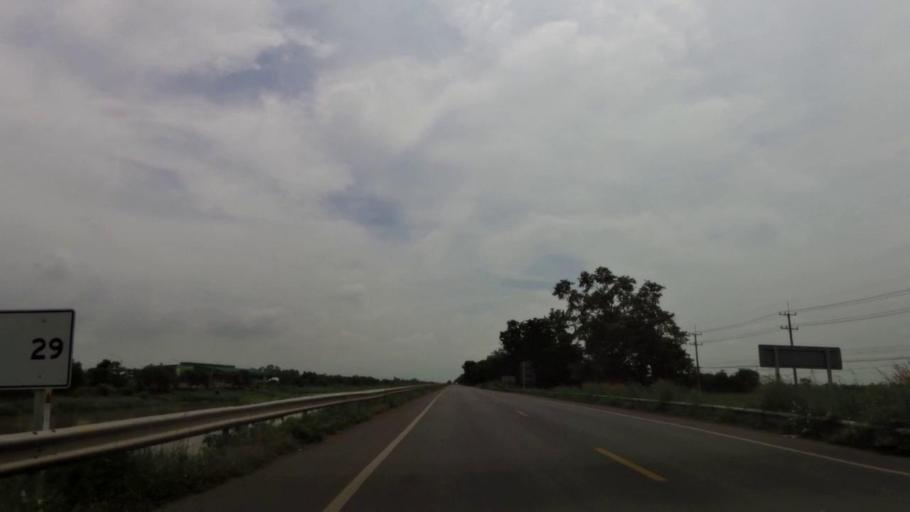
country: TH
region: Lop Buri
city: Ban Mi
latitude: 15.0439
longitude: 100.5646
